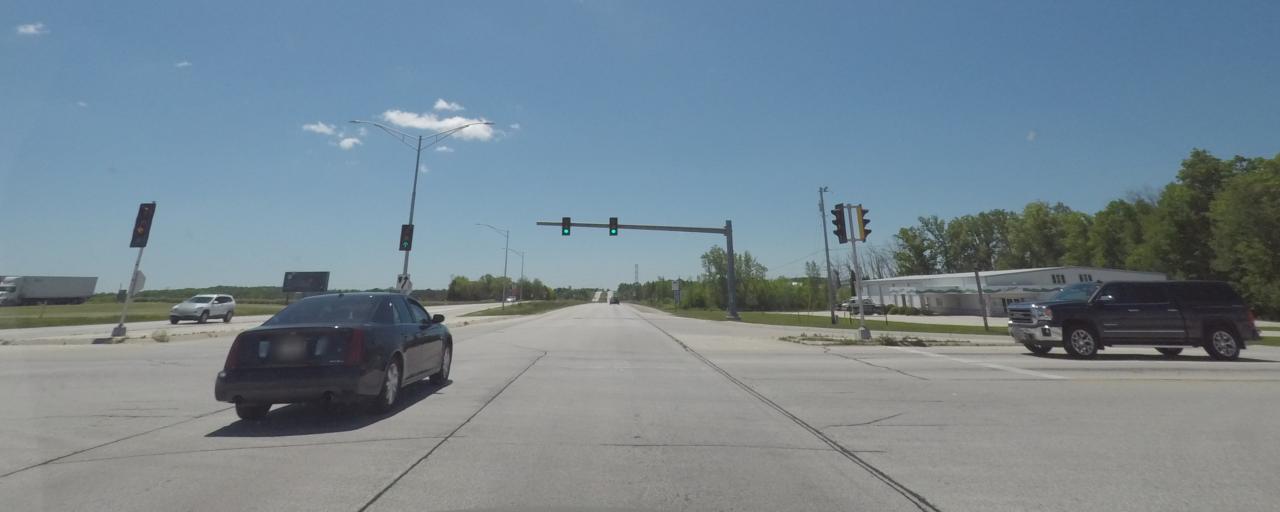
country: US
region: Wisconsin
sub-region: Sheboygan County
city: Plymouth
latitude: 43.7329
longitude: -87.9413
